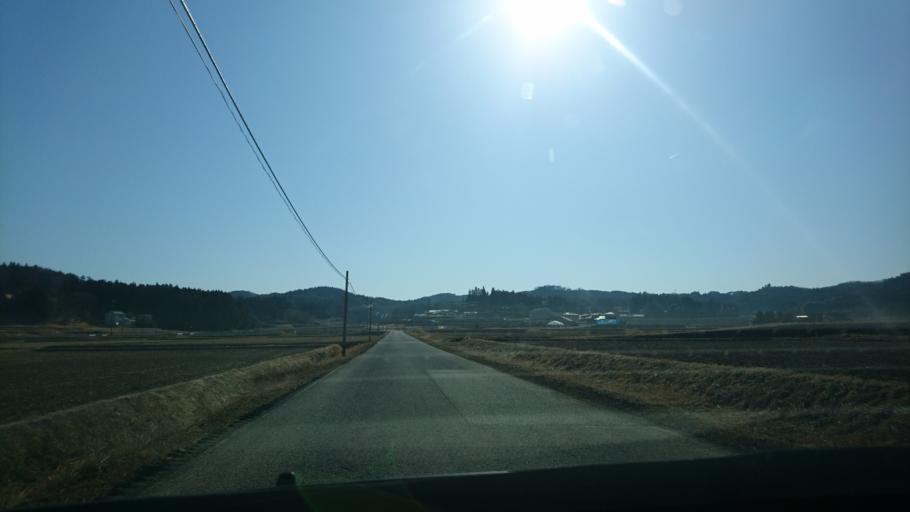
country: JP
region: Iwate
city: Ichinoseki
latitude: 38.8391
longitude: 141.2390
